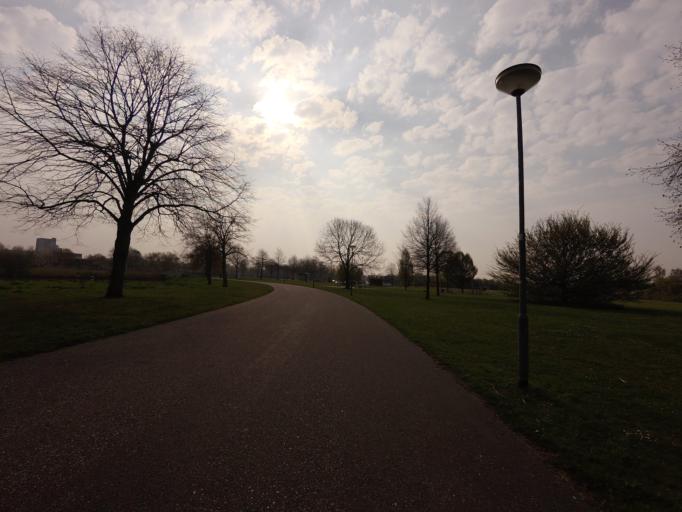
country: NL
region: South Holland
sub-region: Gemeente Rotterdam
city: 's-Gravenland
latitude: 51.9354
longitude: 4.5488
